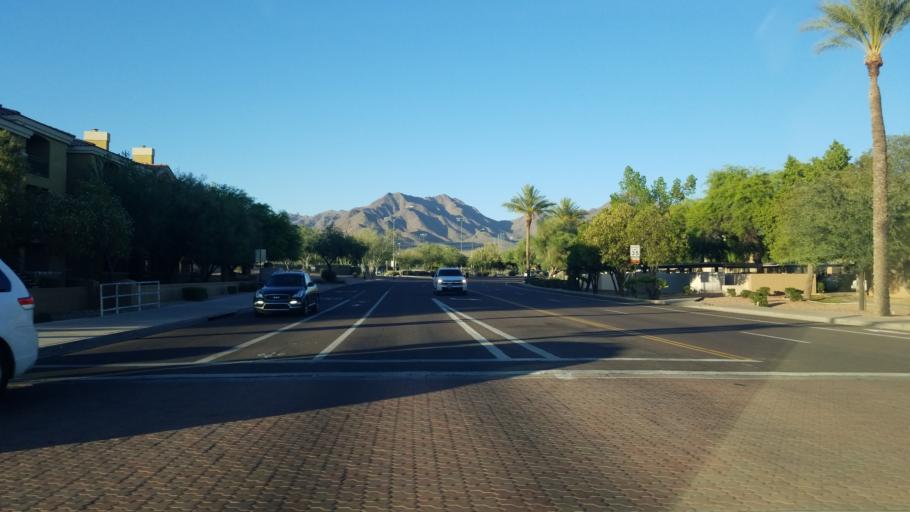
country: US
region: Arizona
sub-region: Maricopa County
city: Paradise Valley
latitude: 33.6258
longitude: -111.8788
